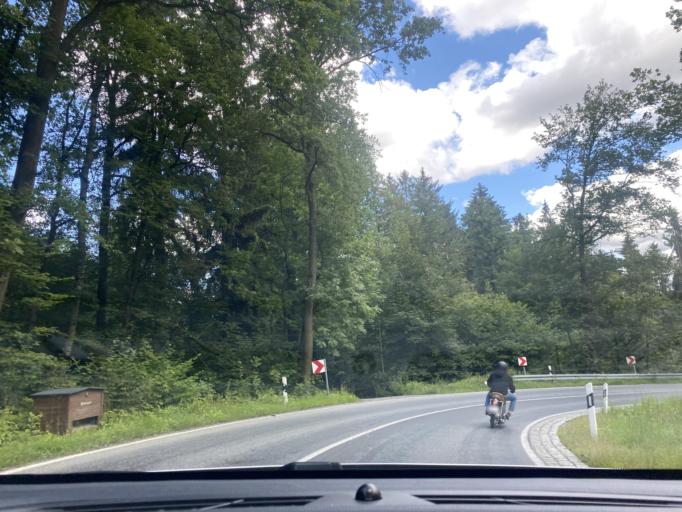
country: DE
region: Saxony
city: Schonbach
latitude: 51.0705
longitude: 14.5831
